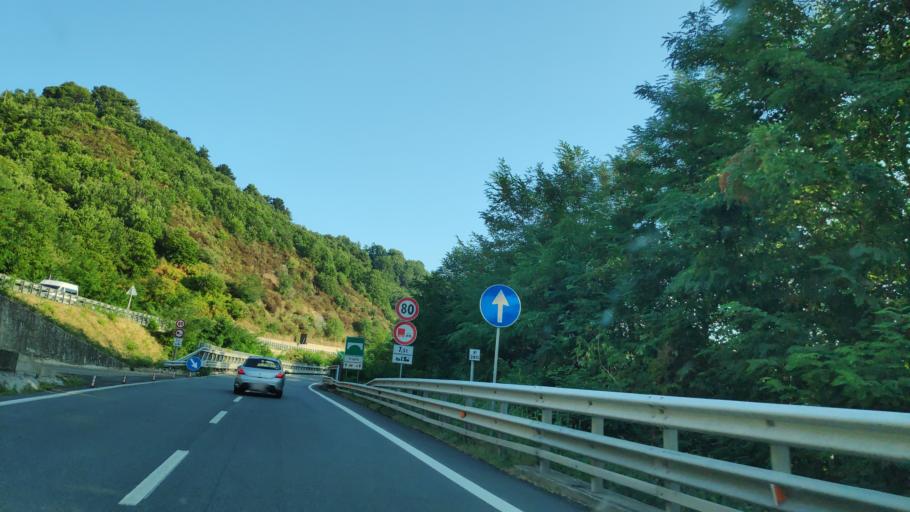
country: IT
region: Calabria
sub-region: Provincia di Cosenza
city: Carpanzano
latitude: 39.1575
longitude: 16.2880
